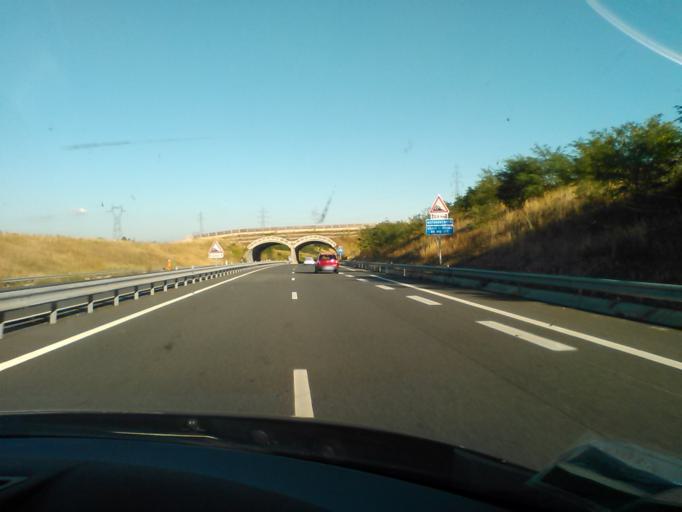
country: FR
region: Rhone-Alpes
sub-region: Departement de l'Ain
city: Beynost
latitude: 45.8525
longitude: 5.0040
